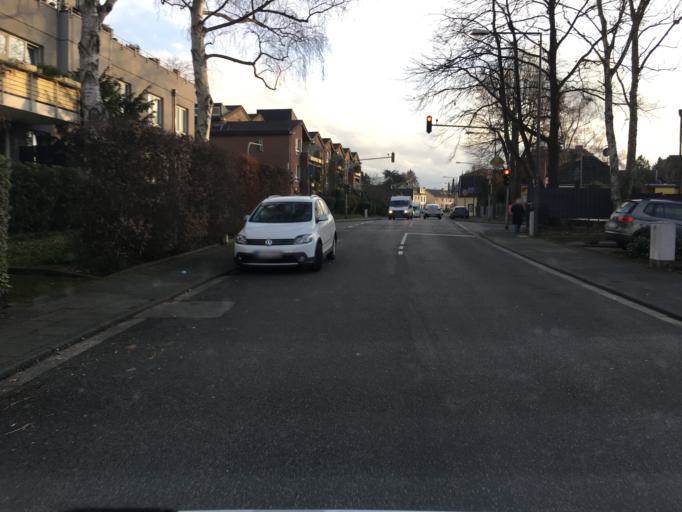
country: DE
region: North Rhine-Westphalia
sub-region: Regierungsbezirk Koln
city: Frechen
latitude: 50.9364
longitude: 6.8267
